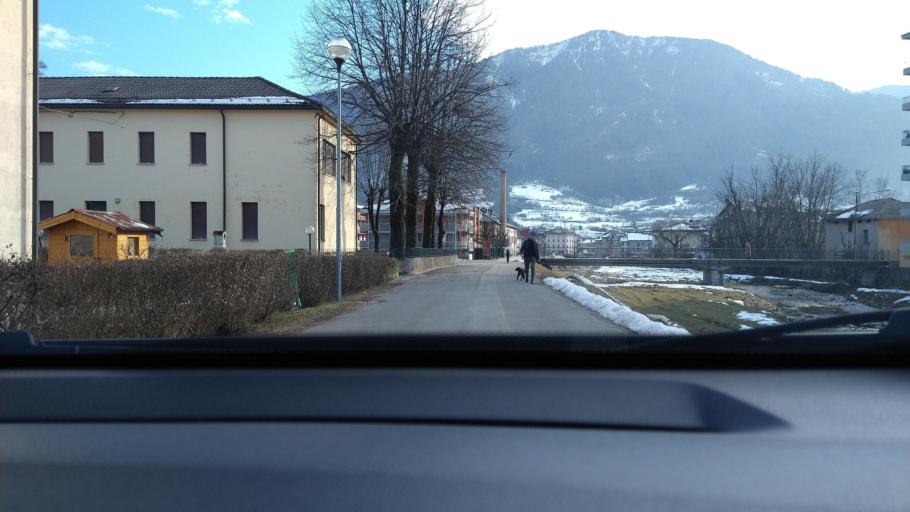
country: IT
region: Veneto
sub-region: Provincia di Belluno
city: Feltre
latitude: 46.0206
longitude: 11.9037
